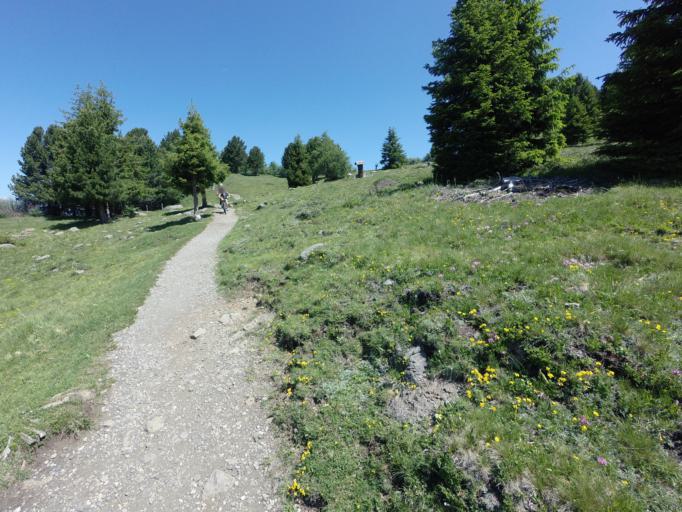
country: IT
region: Trentino-Alto Adige
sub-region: Bolzano
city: Castelrotto
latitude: 46.5622
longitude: 11.6080
